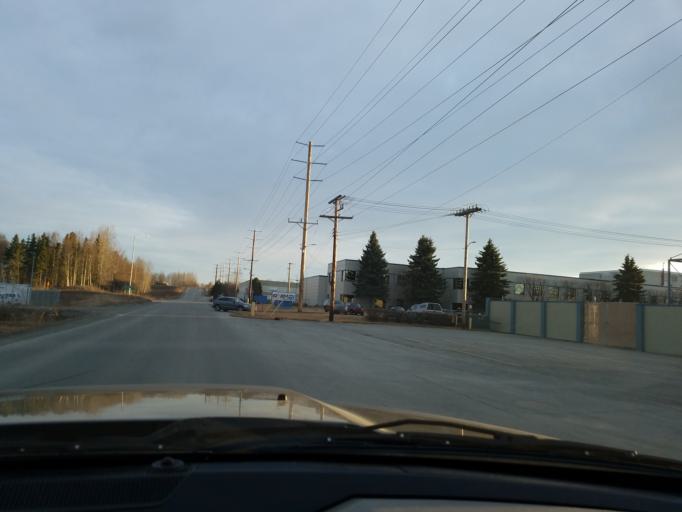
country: US
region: Alaska
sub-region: Anchorage Municipality
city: Anchorage
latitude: 61.1689
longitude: -149.9128
